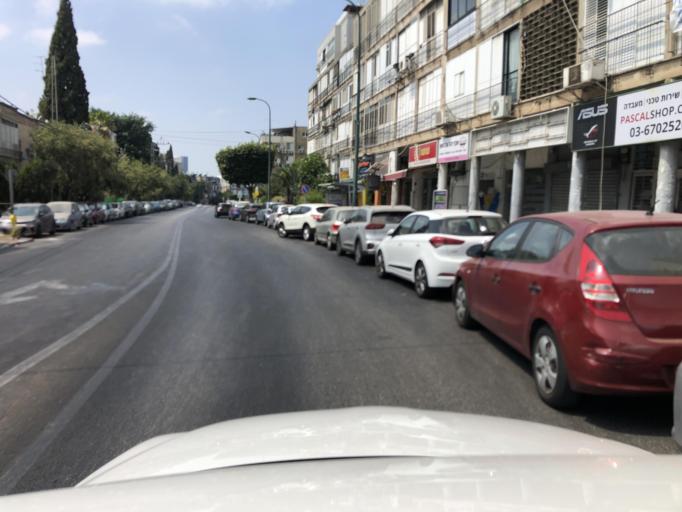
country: IL
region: Tel Aviv
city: Giv`atayim
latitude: 32.0772
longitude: 34.8141
